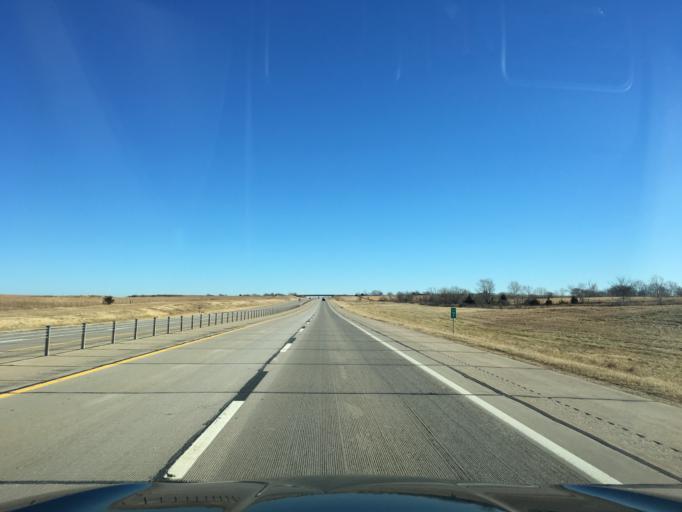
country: US
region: Oklahoma
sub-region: Noble County
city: Perry
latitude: 36.3935
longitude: -97.2047
